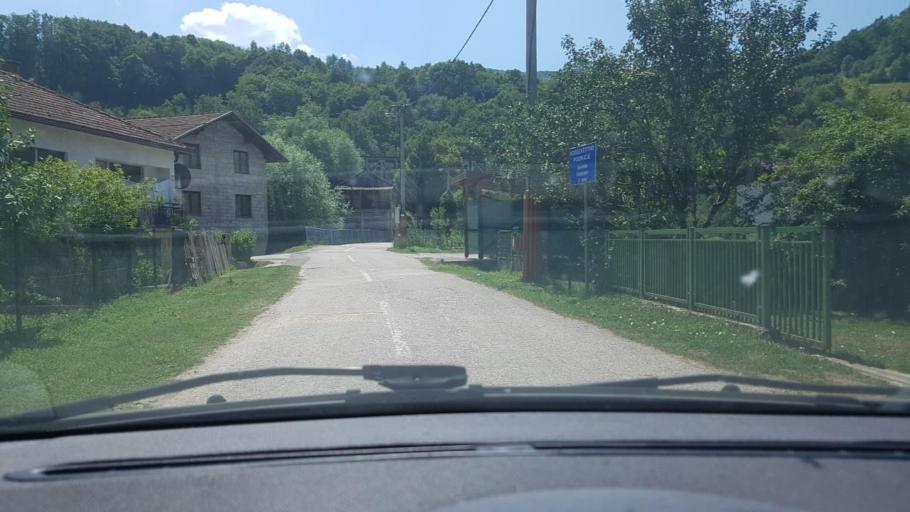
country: BA
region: Federation of Bosnia and Herzegovina
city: Orasac
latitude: 44.5602
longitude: 16.0884
